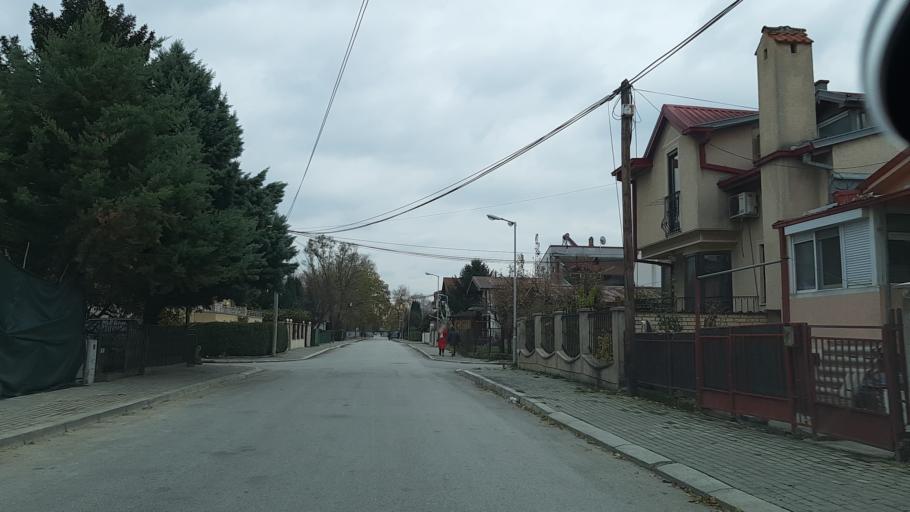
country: MK
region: Kisela Voda
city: Usje
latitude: 41.9766
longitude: 21.4699
